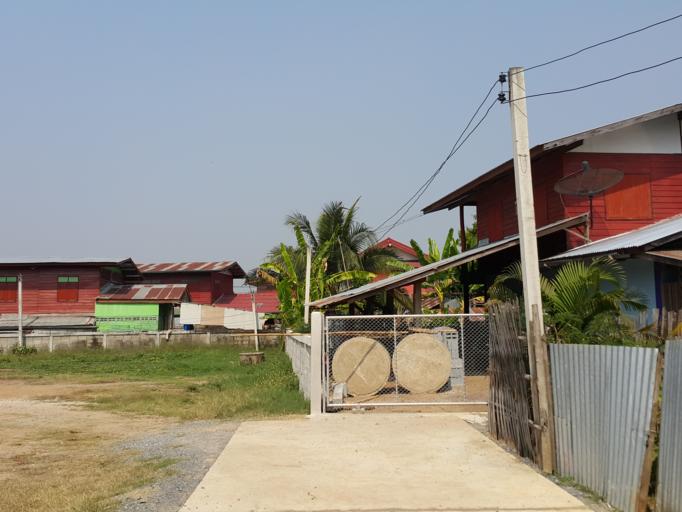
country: TH
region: Sukhothai
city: Thung Saliam
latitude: 17.3249
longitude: 99.5131
